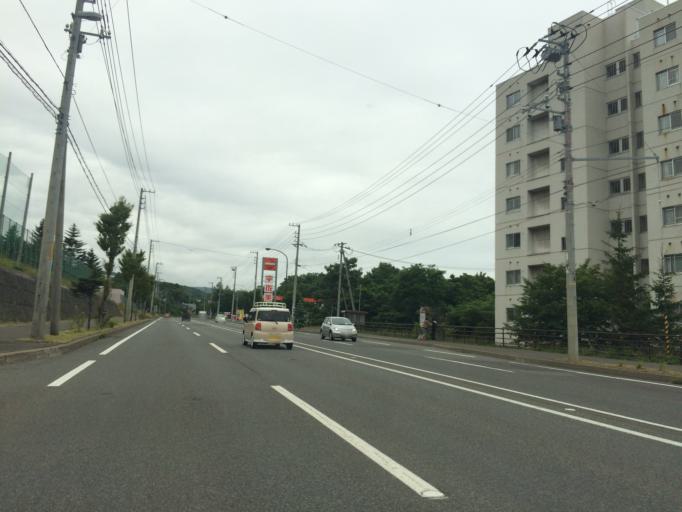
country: JP
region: Hokkaido
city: Otaru
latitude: 43.1400
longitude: 141.1559
